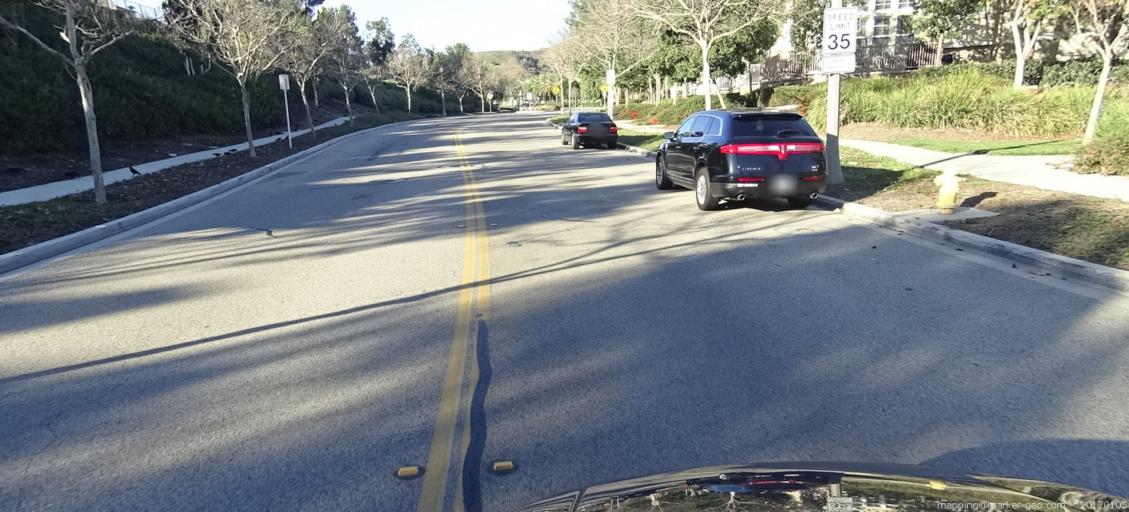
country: US
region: California
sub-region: Orange County
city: Ladera Ranch
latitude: 33.5441
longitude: -117.6477
